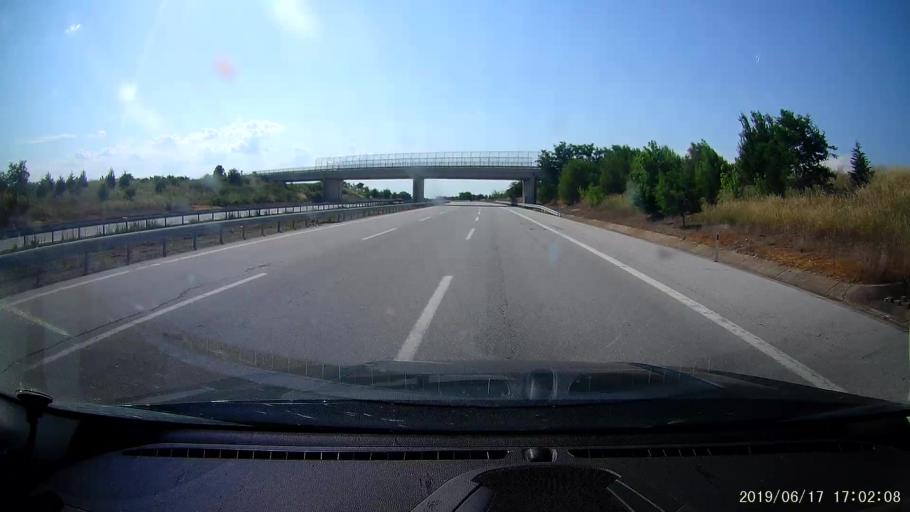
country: TR
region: Edirne
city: Haskoy
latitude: 41.6367
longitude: 26.7884
